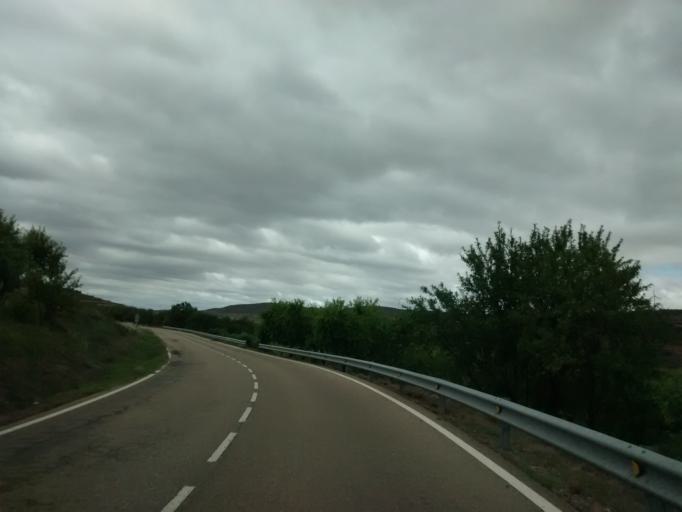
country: ES
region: Aragon
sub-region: Provincia de Zaragoza
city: Trasmoz
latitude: 41.8380
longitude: -1.7105
